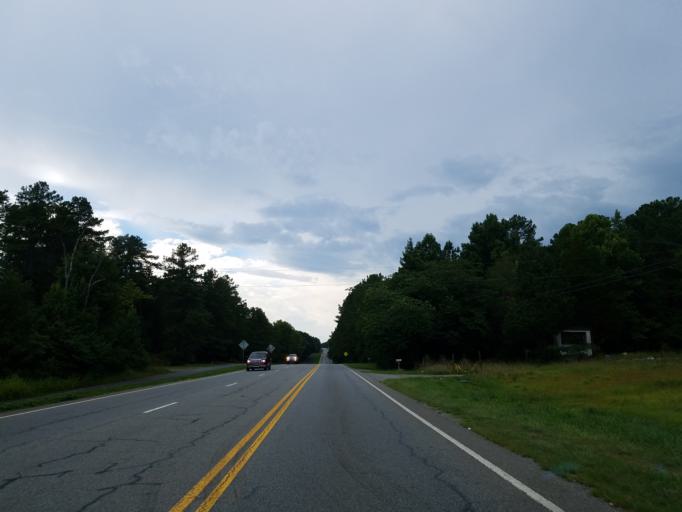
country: US
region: Georgia
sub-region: Bartow County
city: Adairsville
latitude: 34.2888
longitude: -84.8730
